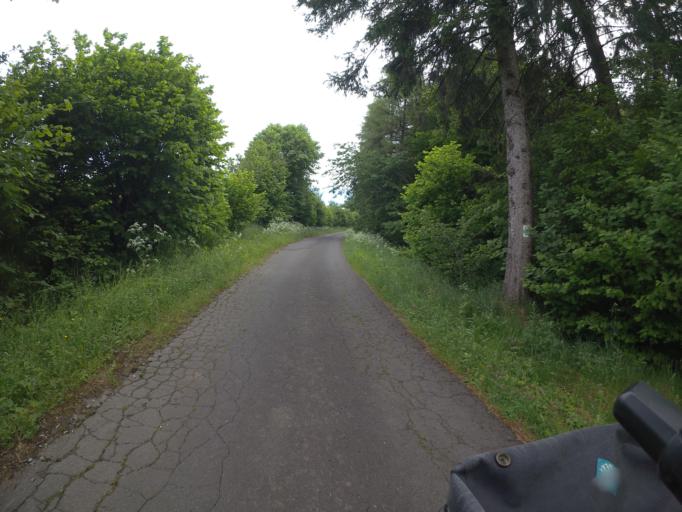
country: DE
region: Rheinland-Pfalz
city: Scheid
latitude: 50.4046
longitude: 6.3907
